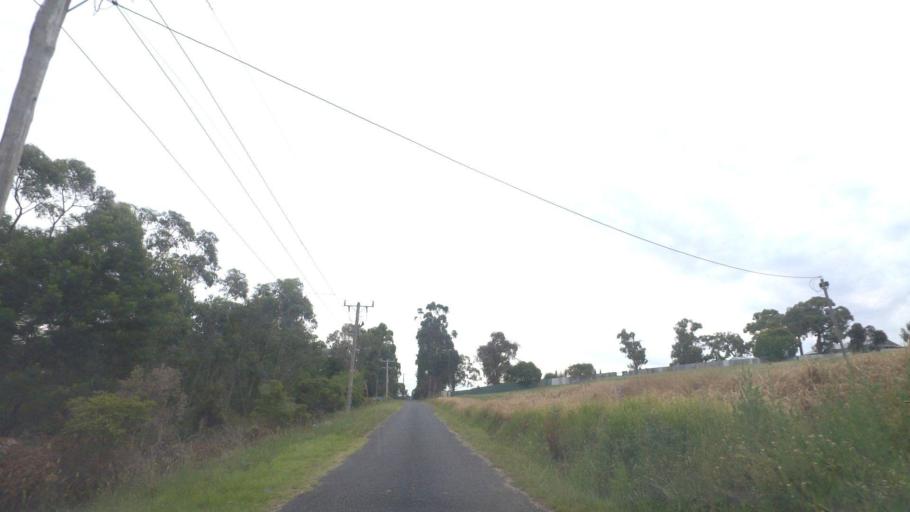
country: AU
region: Victoria
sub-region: Yarra Ranges
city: Mount Evelyn
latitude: -37.7687
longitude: 145.4002
